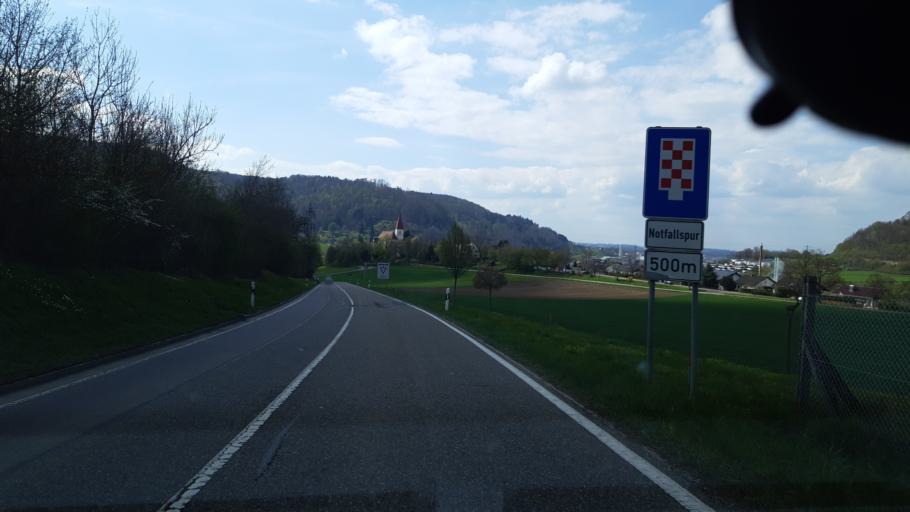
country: DE
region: Baden-Wuerttemberg
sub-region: Regierungsbezirk Stuttgart
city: Oberkochen
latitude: 48.8124
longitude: 10.1388
